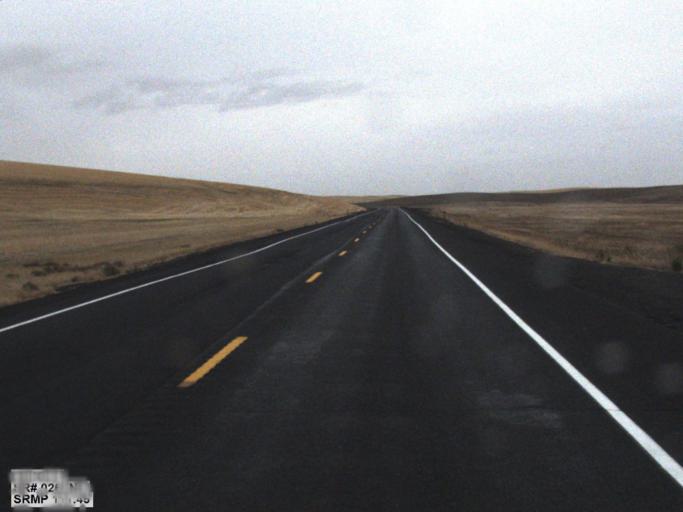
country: US
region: Washington
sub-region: Garfield County
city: Pomeroy
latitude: 46.8032
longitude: -117.7648
